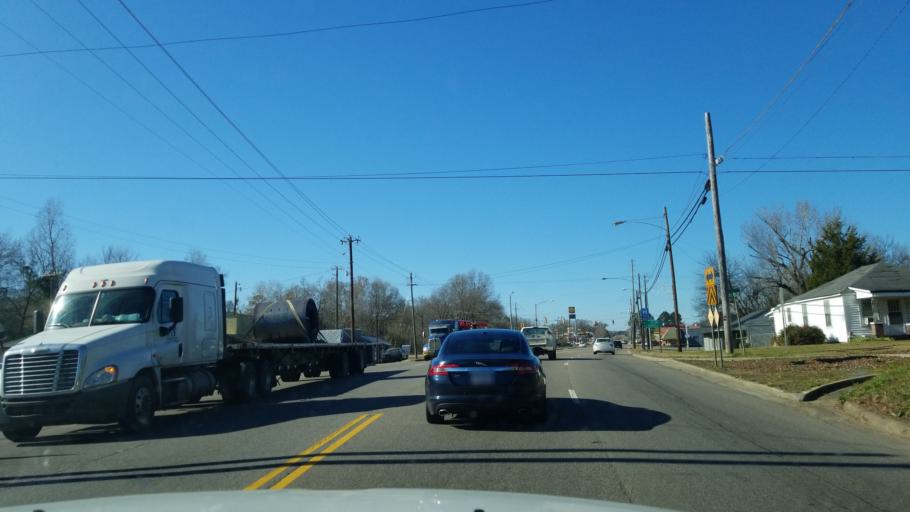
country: US
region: Alabama
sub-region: Pickens County
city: Reform
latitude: 33.3789
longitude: -88.0160
